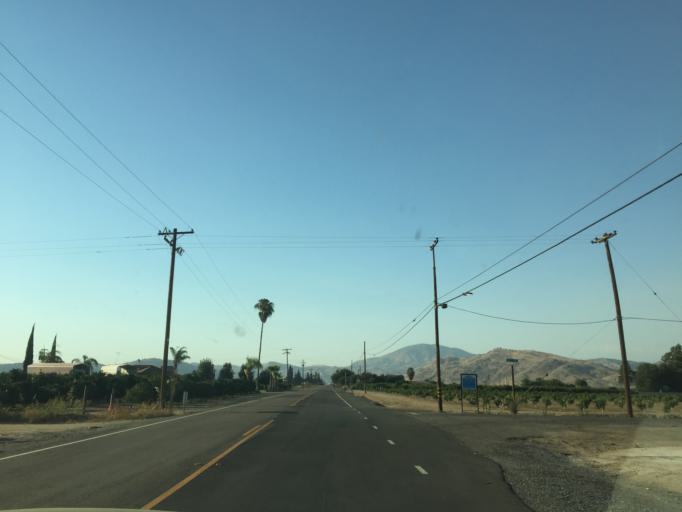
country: US
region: California
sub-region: Fresno County
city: Orange Cove
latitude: 36.6384
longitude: -119.3047
